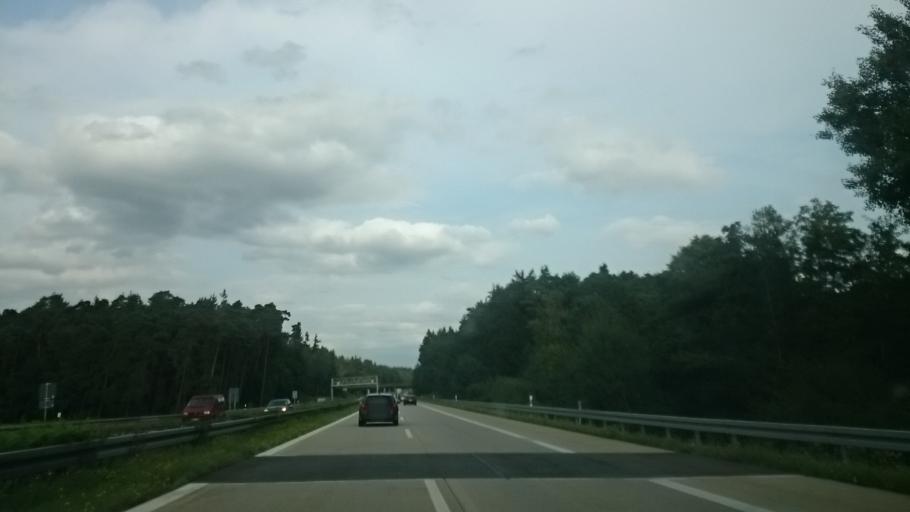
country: DE
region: Bavaria
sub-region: Lower Bavaria
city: Hausen
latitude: 48.8355
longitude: 11.9817
